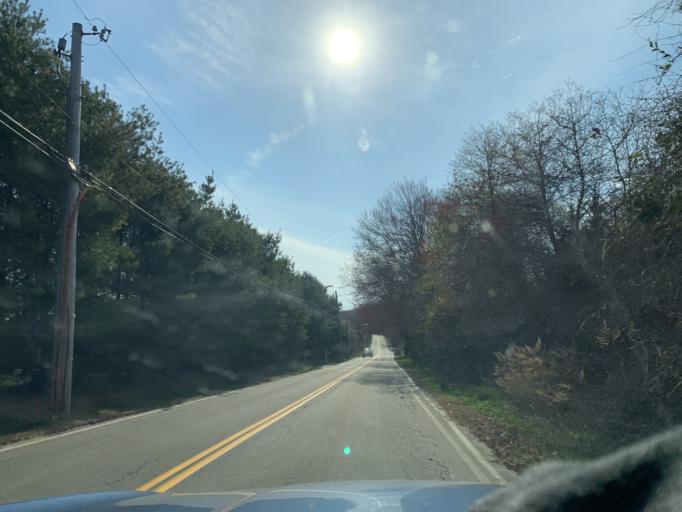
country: US
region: Rhode Island
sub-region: Kent County
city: West Warwick
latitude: 41.7507
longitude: -71.5166
